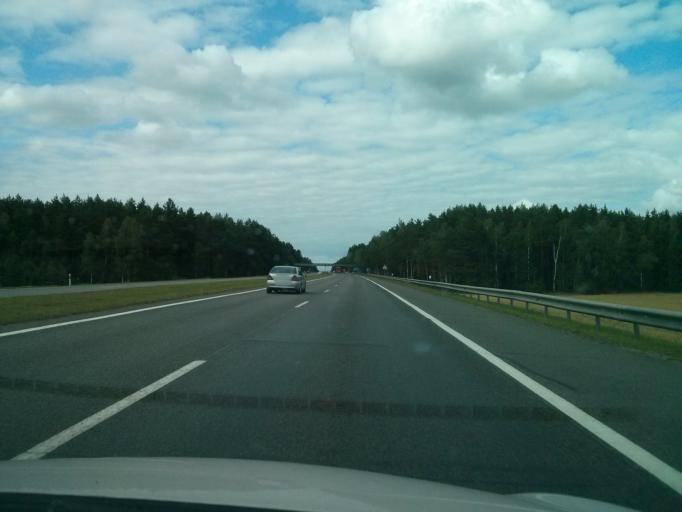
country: BY
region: Minsk
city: Zamostochcha
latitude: 53.8881
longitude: 27.9399
